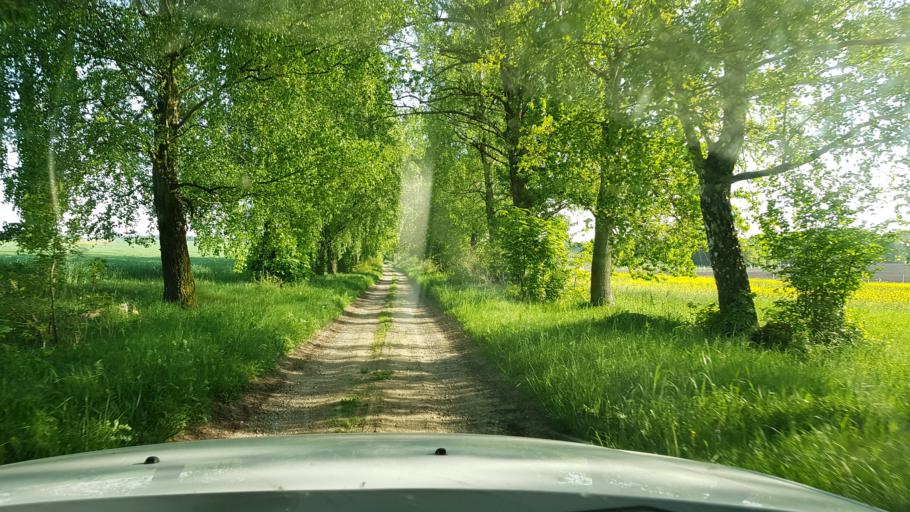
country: PL
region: West Pomeranian Voivodeship
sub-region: Powiat lobeski
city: Resko
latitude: 53.6997
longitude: 15.3365
